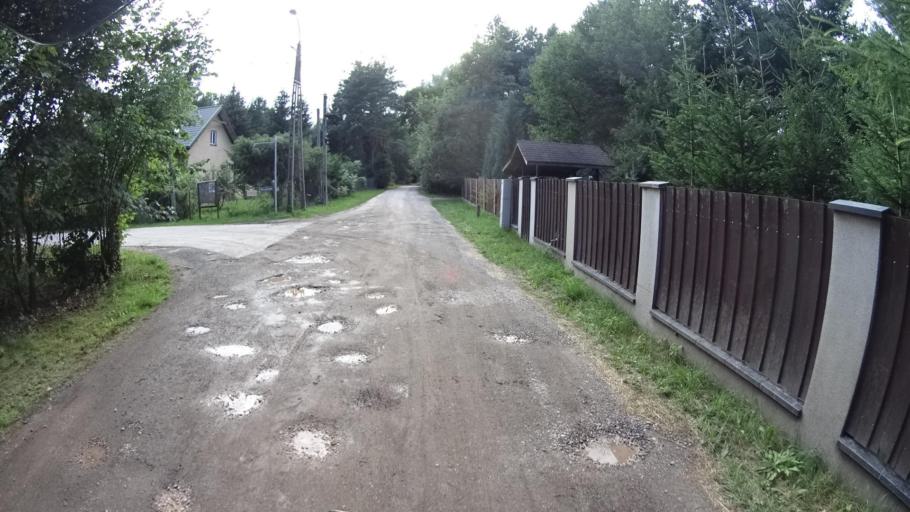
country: PL
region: Masovian Voivodeship
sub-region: Powiat piaseczynski
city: Tarczyn
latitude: 51.9757
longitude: 20.8699
